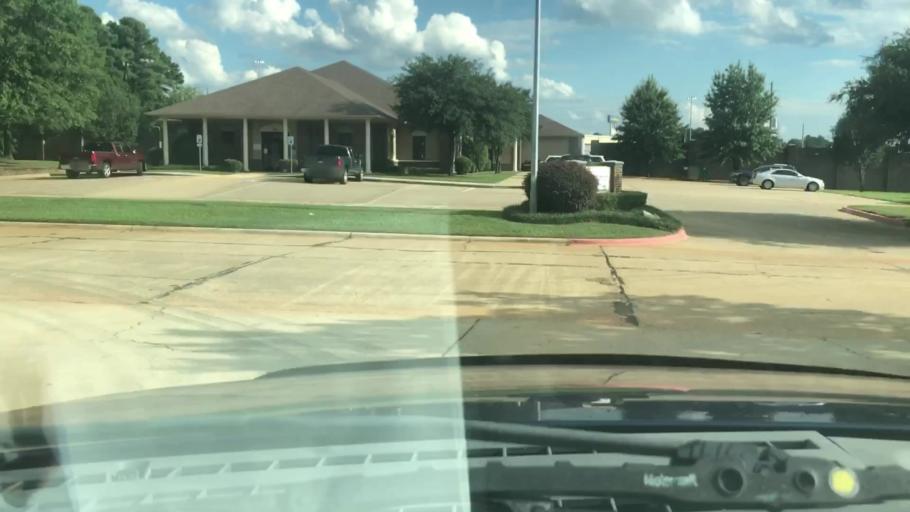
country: US
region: Arkansas
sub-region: Miller County
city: Texarkana
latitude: 33.4703
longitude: -94.0648
